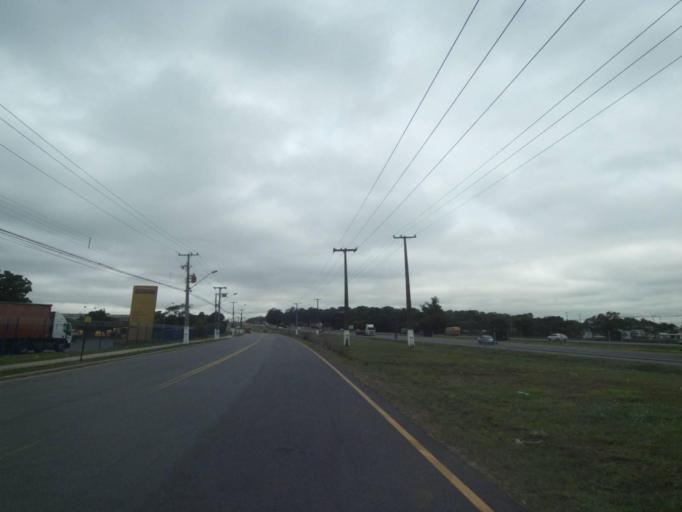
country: BR
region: Parana
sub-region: Araucaria
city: Araucaria
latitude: -25.5295
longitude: -49.3261
